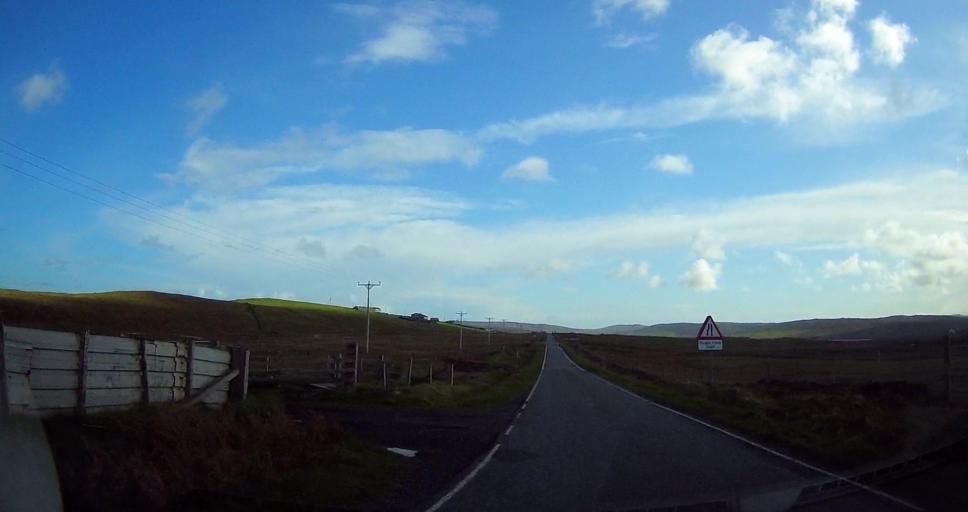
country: GB
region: Scotland
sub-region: Shetland Islands
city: Shetland
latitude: 60.3615
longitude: -1.1431
